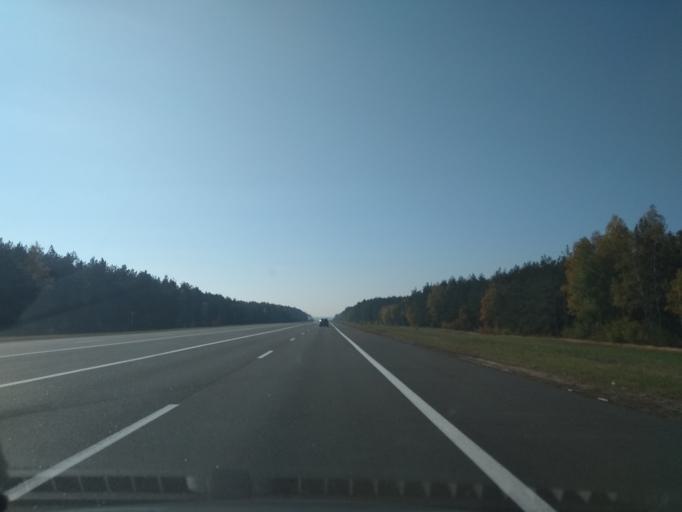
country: BY
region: Brest
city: Ivatsevichy
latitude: 52.7559
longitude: 25.5101
